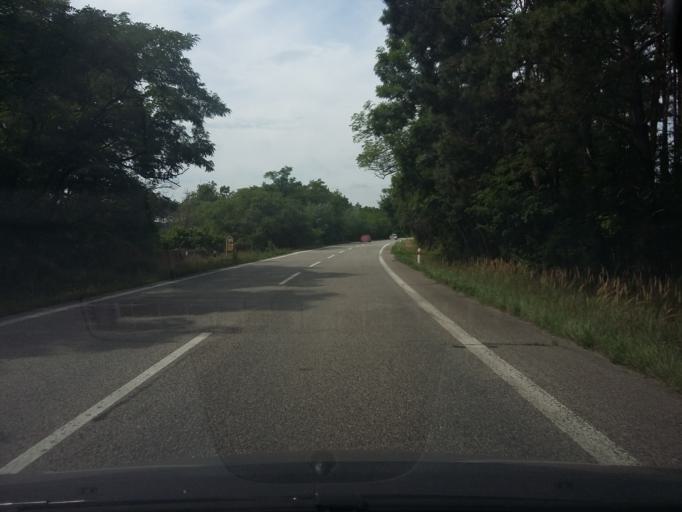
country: SK
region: Bratislavsky
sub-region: Okres Malacky
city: Malacky
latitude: 48.3882
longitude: 17.1008
